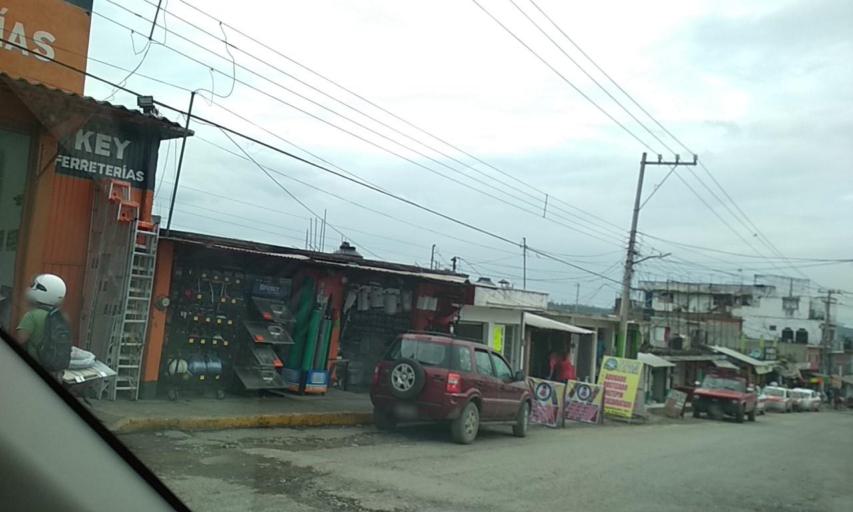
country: MX
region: Veracruz
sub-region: Papantla
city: El Chote
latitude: 20.4025
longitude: -97.3396
